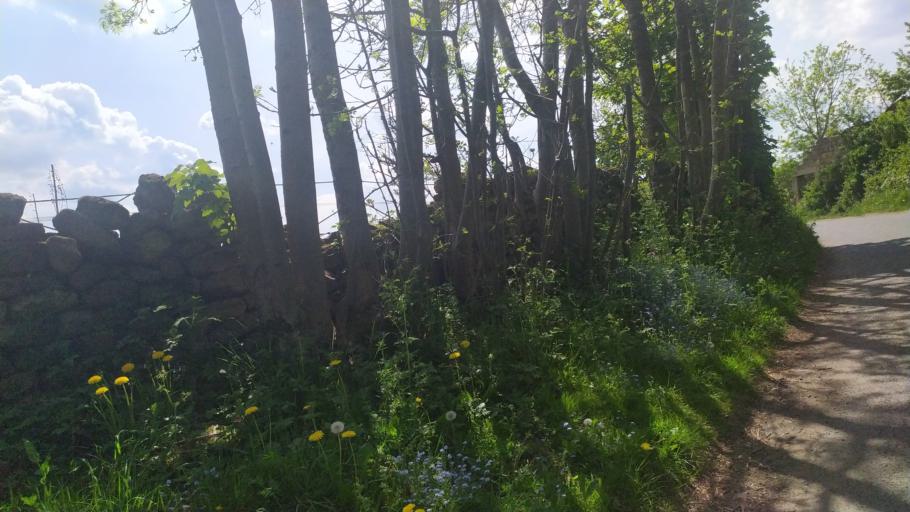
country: GB
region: England
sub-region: City and Borough of Leeds
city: Chapel Allerton
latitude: 53.8756
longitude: -1.5620
